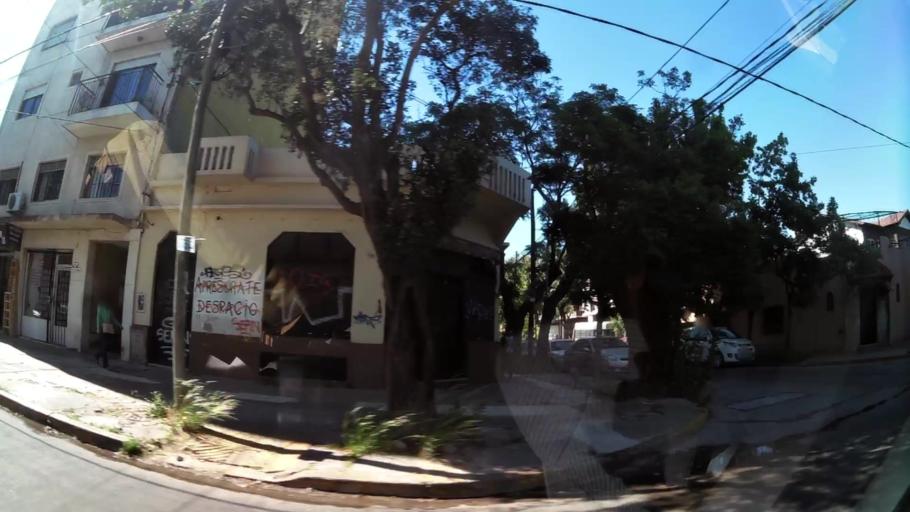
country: AR
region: Buenos Aires
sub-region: Partido de Vicente Lopez
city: Olivos
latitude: -34.5411
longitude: -58.4896
